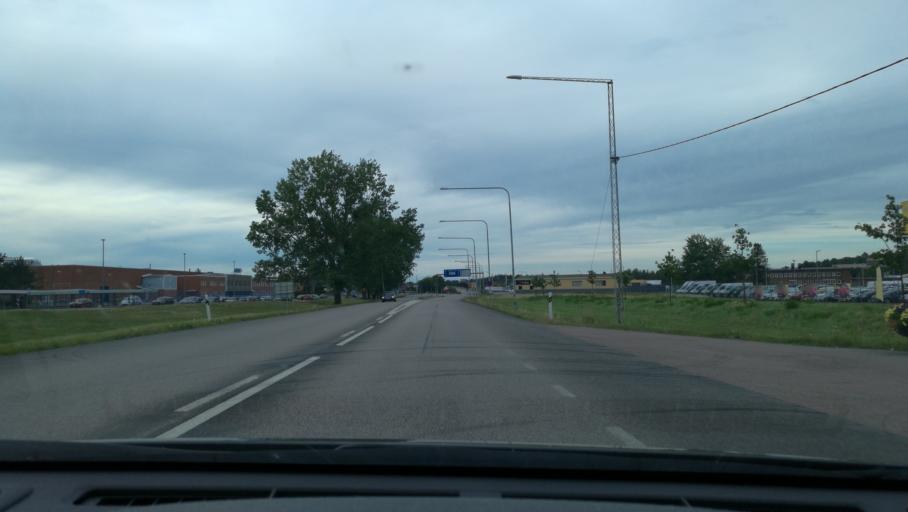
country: SE
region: Vaestmanland
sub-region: Kopings Kommun
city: Koping
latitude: 59.5013
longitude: 15.9938
